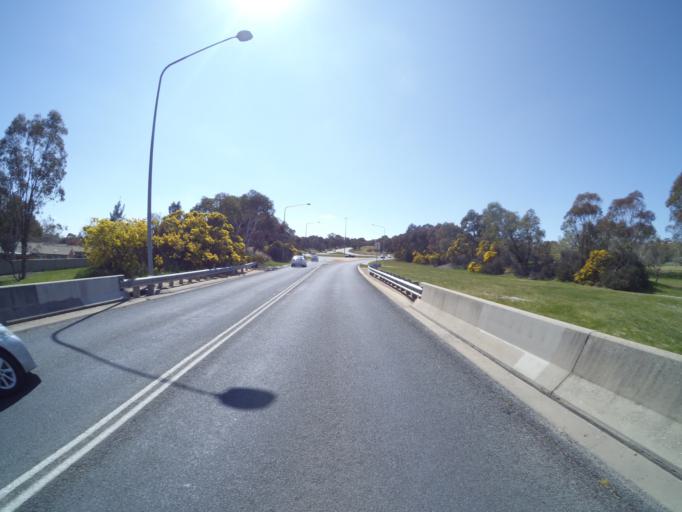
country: AU
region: Australian Capital Territory
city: Macarthur
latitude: -35.4354
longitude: 149.0943
